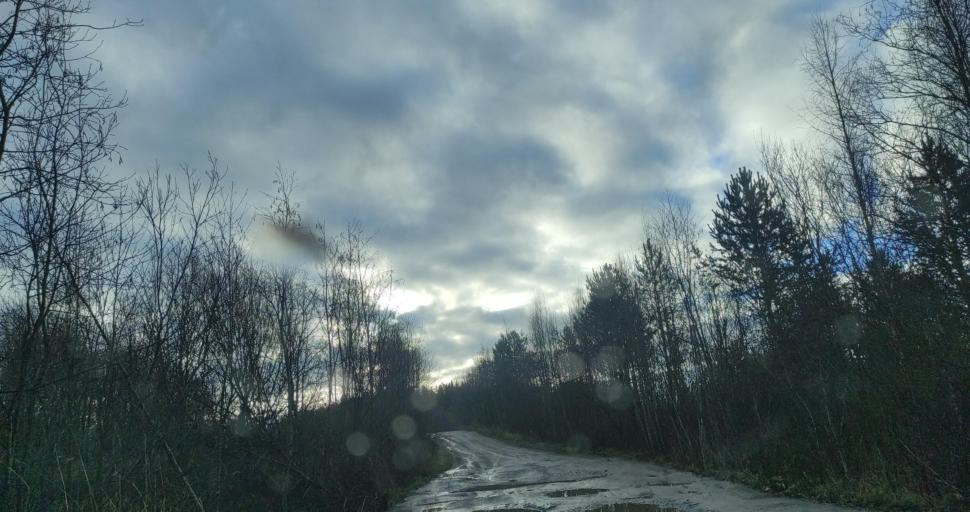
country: RU
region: Republic of Karelia
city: Pitkyaranta
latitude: 61.7317
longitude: 31.3865
